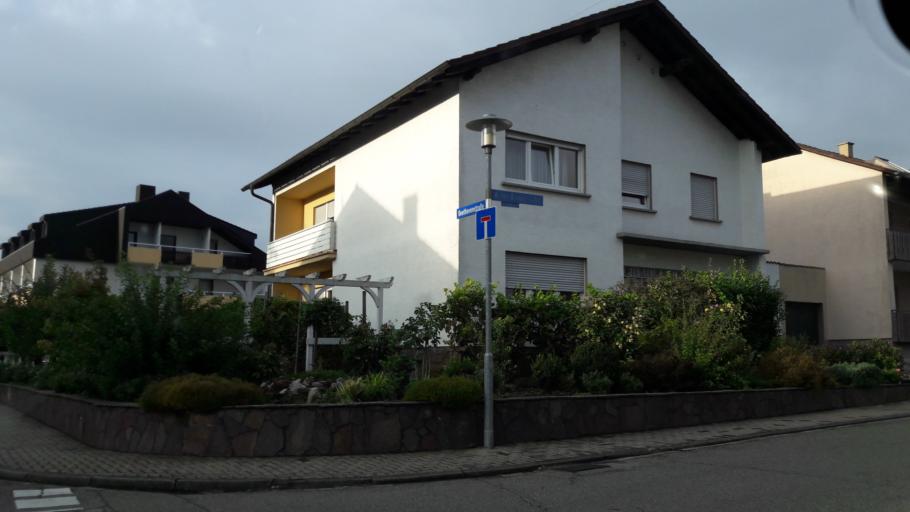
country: DE
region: Baden-Wuerttemberg
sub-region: Karlsruhe Region
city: Malsch
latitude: 49.2225
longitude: 8.6635
